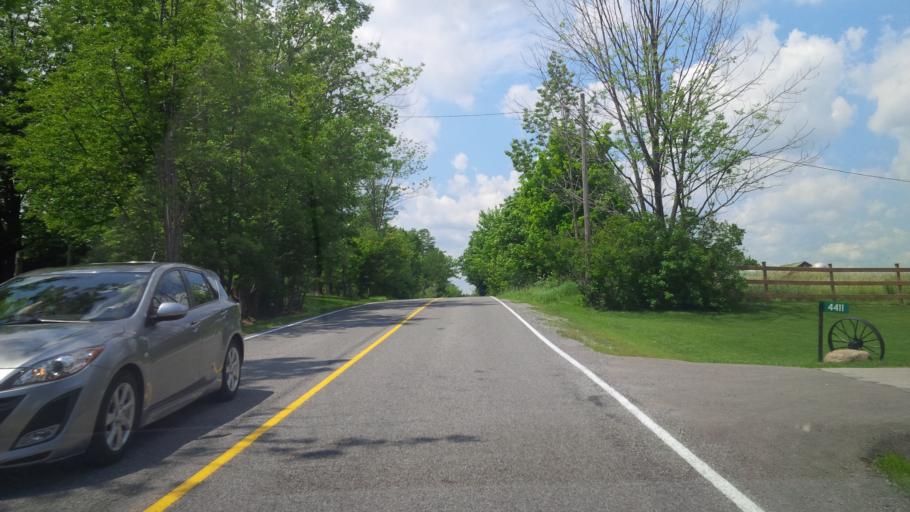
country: CA
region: Ontario
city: Burlington
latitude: 43.4159
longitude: -79.8556
